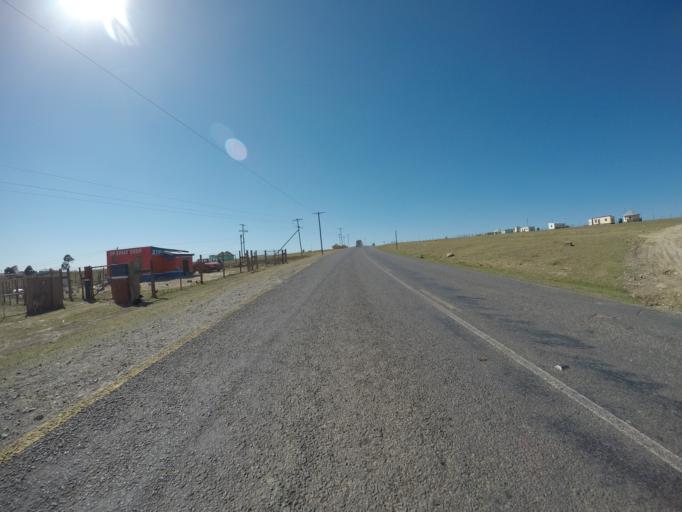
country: ZA
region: Eastern Cape
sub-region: OR Tambo District Municipality
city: Mthatha
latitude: -31.8836
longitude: 28.7579
